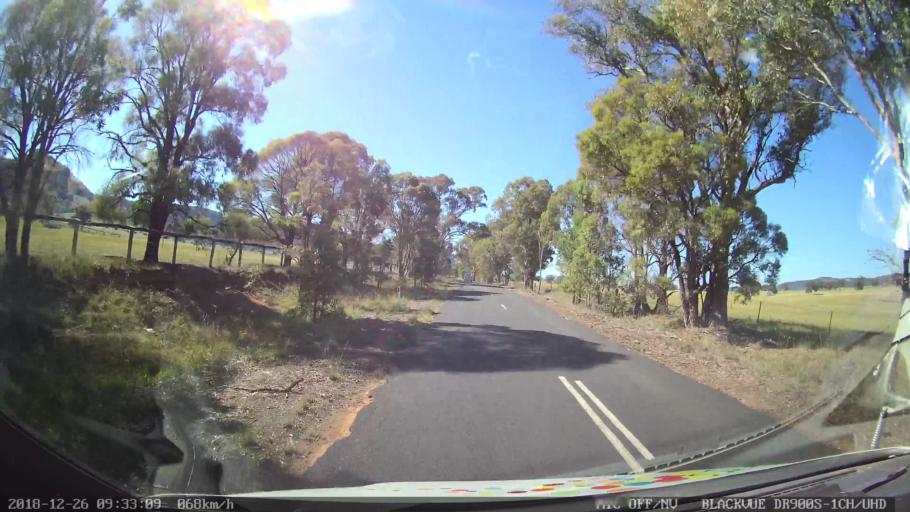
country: AU
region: New South Wales
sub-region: Mid-Western Regional
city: Kandos
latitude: -32.8918
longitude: 150.0340
